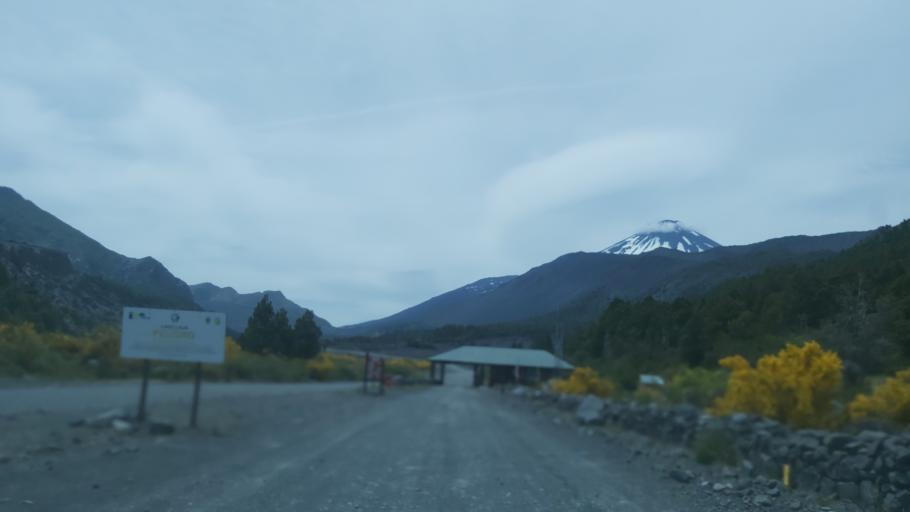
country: AR
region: Neuquen
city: Andacollo
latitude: -37.3984
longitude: -71.4410
